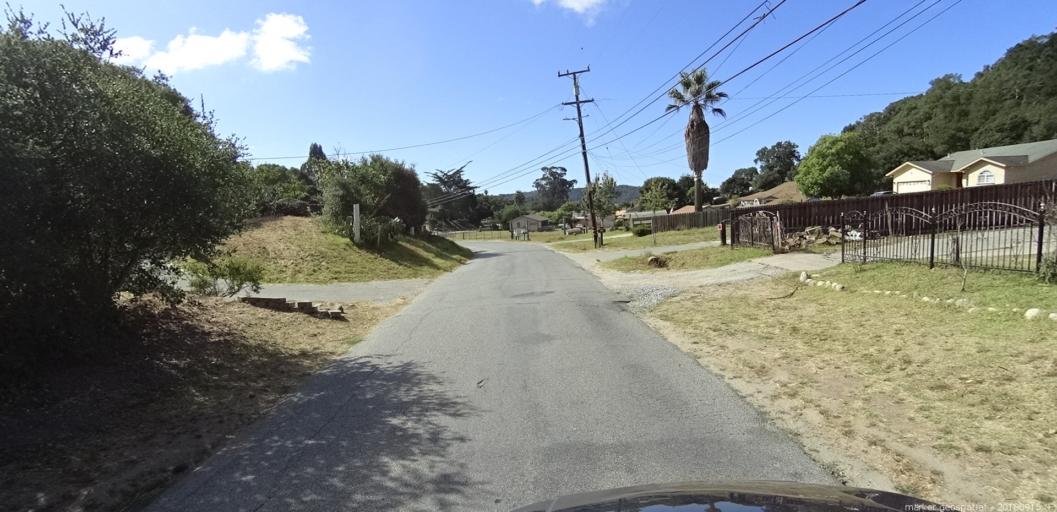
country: US
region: California
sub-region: Monterey County
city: Las Lomas
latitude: 36.8762
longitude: -121.7350
